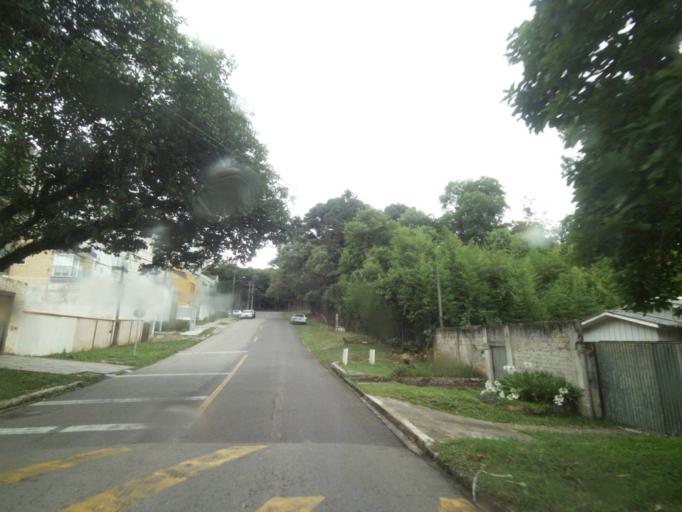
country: BR
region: Parana
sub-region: Curitiba
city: Curitiba
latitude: -25.4451
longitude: -49.3227
